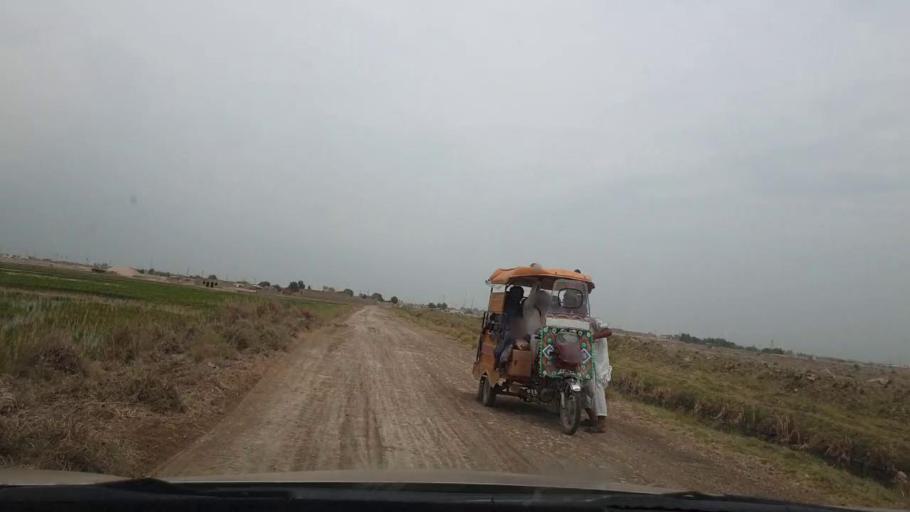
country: PK
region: Sindh
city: Ratodero
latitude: 27.7795
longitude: 68.2803
